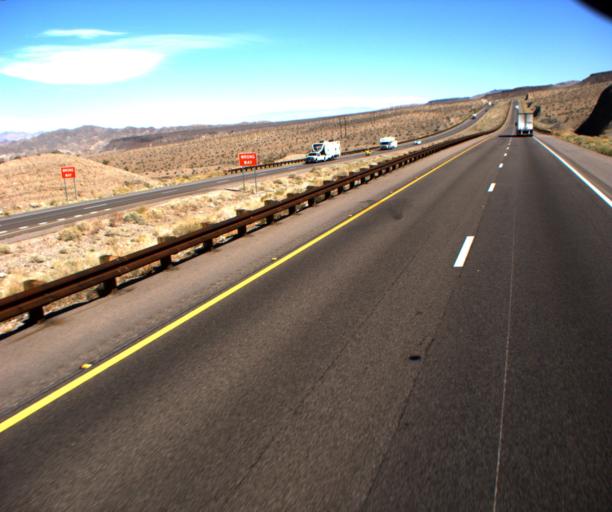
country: US
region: Nevada
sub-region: Clark County
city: Boulder City
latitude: 35.9171
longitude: -114.6299
